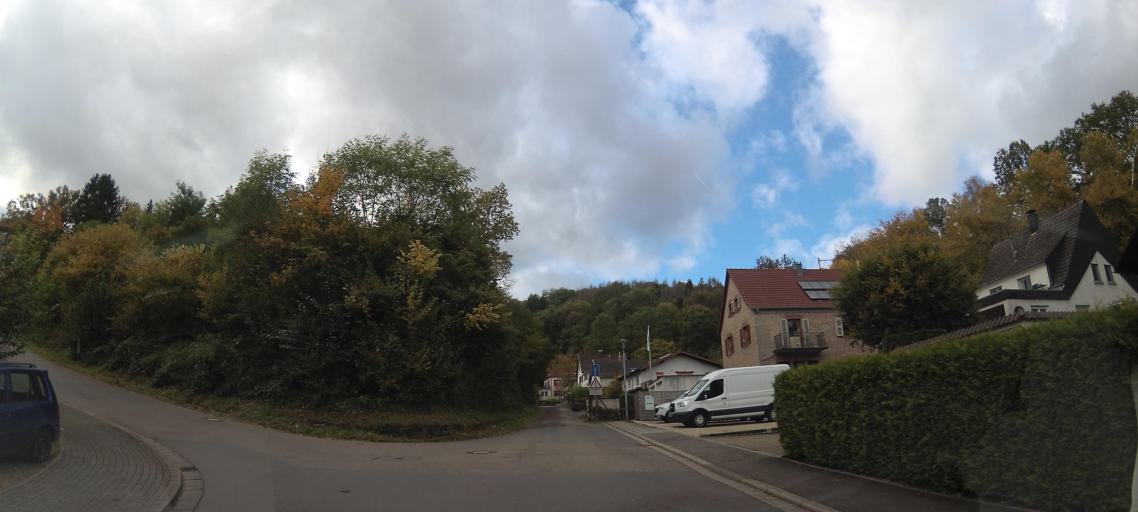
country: DE
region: Saarland
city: Blieskastel
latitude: 49.2431
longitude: 7.2548
